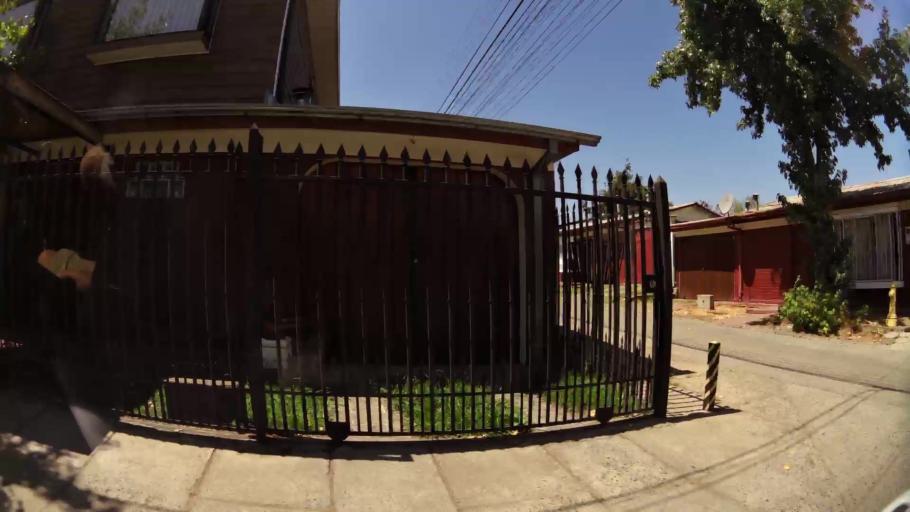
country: CL
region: Maule
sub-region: Provincia de Talca
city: Talca
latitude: -35.4281
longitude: -71.6307
